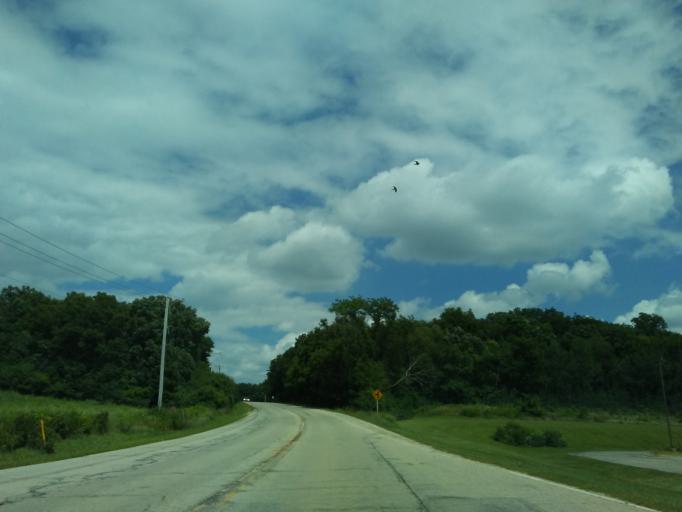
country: US
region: Wisconsin
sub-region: Dane County
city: Verona
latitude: 43.0139
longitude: -89.5558
